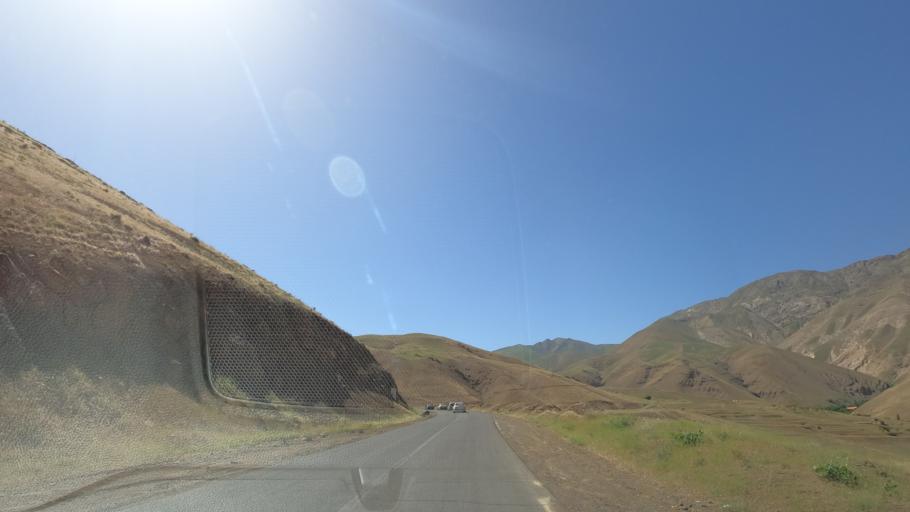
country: IR
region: Alborz
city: Karaj
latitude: 35.9273
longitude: 51.0951
